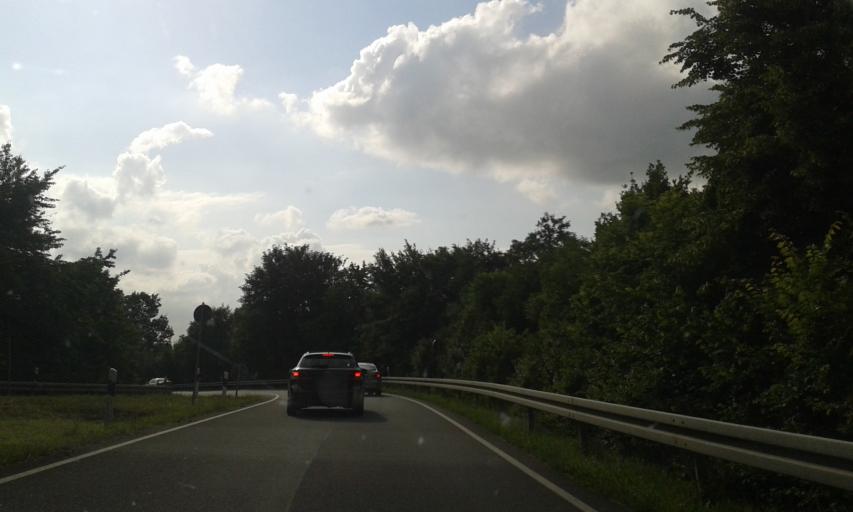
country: DE
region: Lower Saxony
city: Rinteln
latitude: 52.1738
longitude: 9.0857
